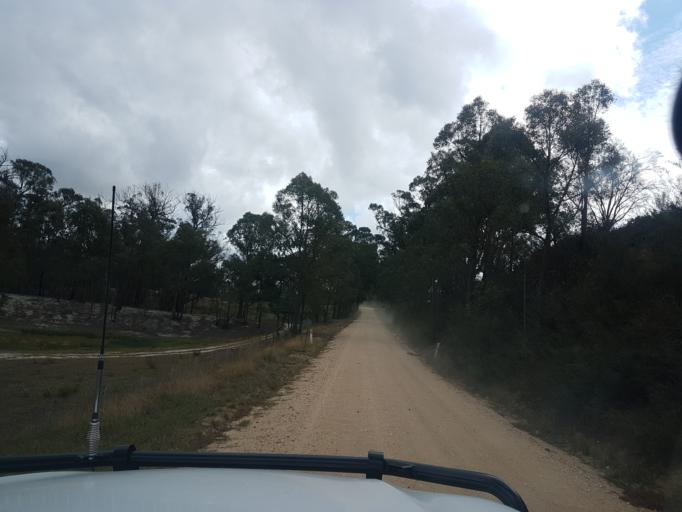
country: AU
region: Victoria
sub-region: East Gippsland
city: Bairnsdale
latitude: -37.7843
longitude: 147.5354
